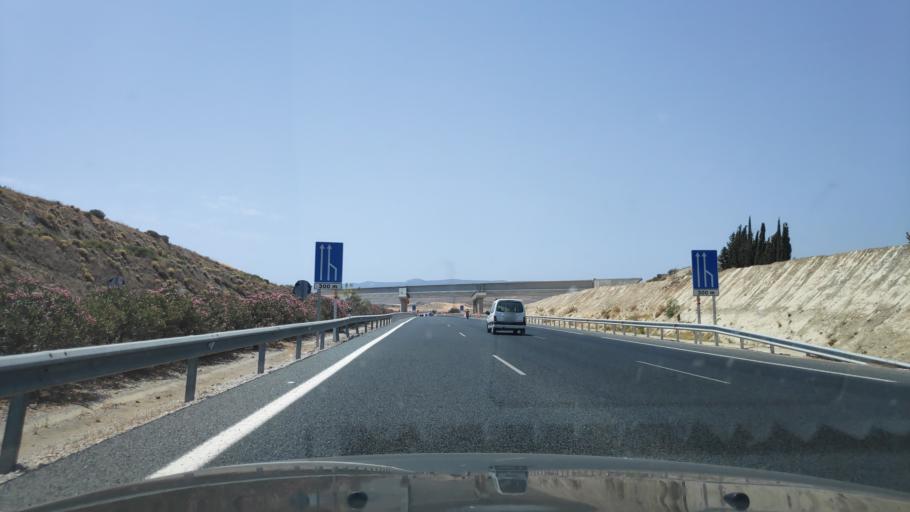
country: ES
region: Andalusia
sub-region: Provincia de Granada
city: Otura
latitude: 37.0673
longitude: -3.6518
